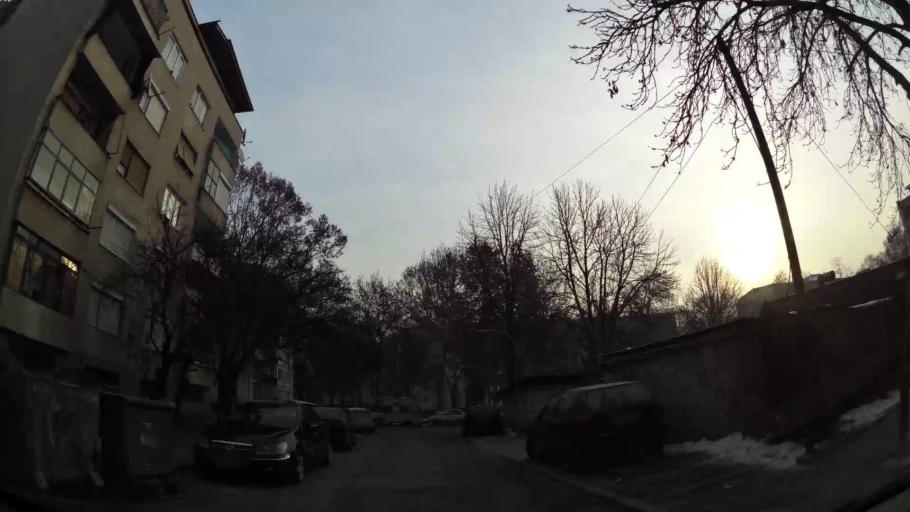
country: MK
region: Cair
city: Cair
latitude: 42.0172
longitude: 21.4457
